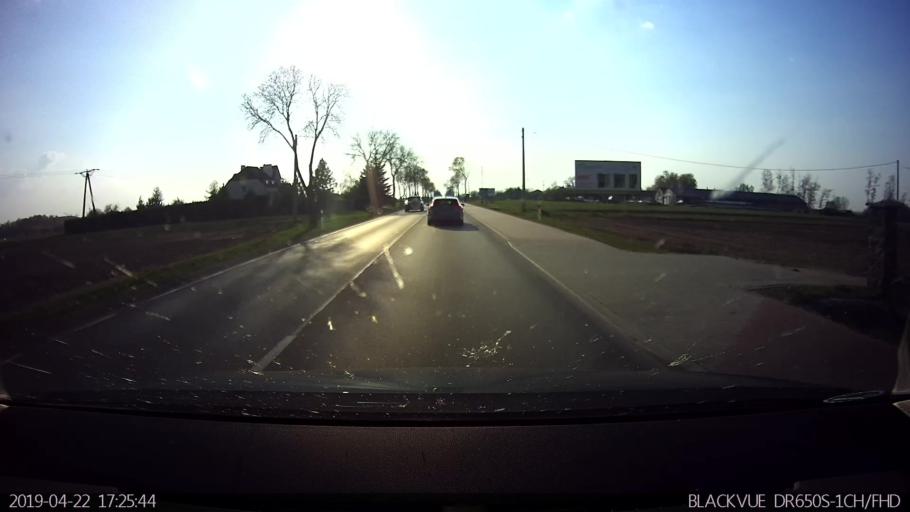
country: PL
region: Masovian Voivodeship
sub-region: Powiat sokolowski
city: Sokolow Podlaski
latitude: 52.3944
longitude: 22.2863
